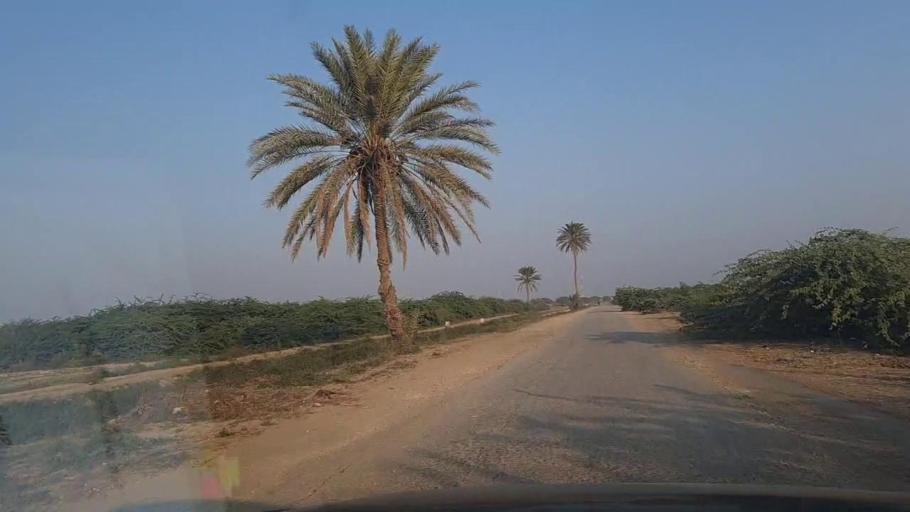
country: PK
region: Sindh
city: Keti Bandar
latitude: 24.3008
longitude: 67.5933
